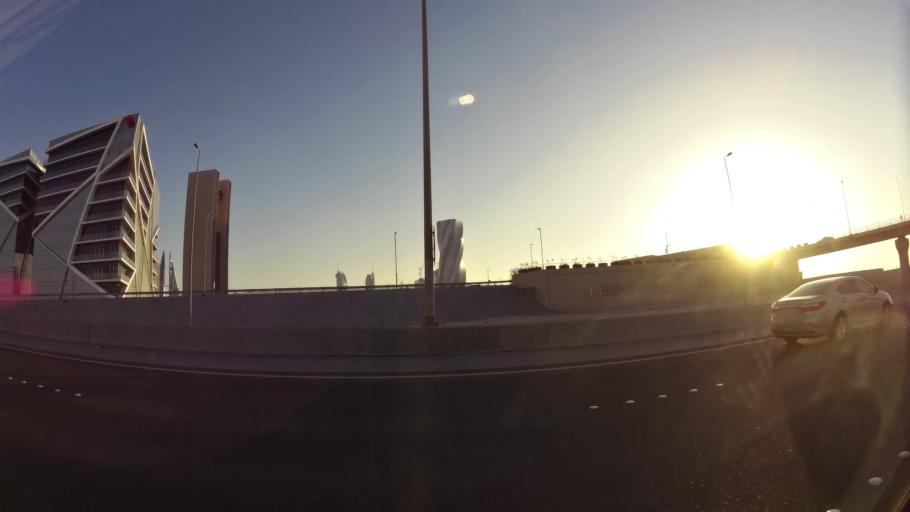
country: BH
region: Muharraq
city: Al Muharraq
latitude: 26.2524
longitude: 50.5826
